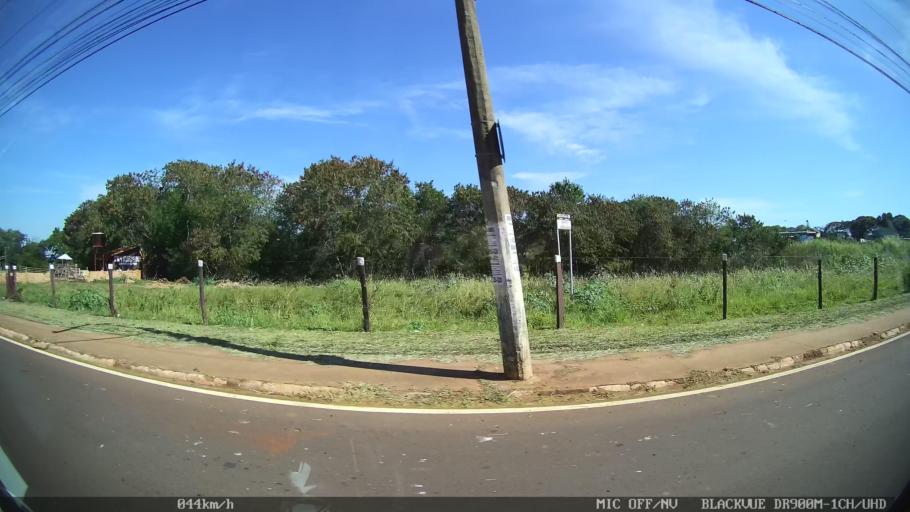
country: BR
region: Sao Paulo
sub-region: Franca
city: Franca
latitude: -20.5445
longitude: -47.4211
